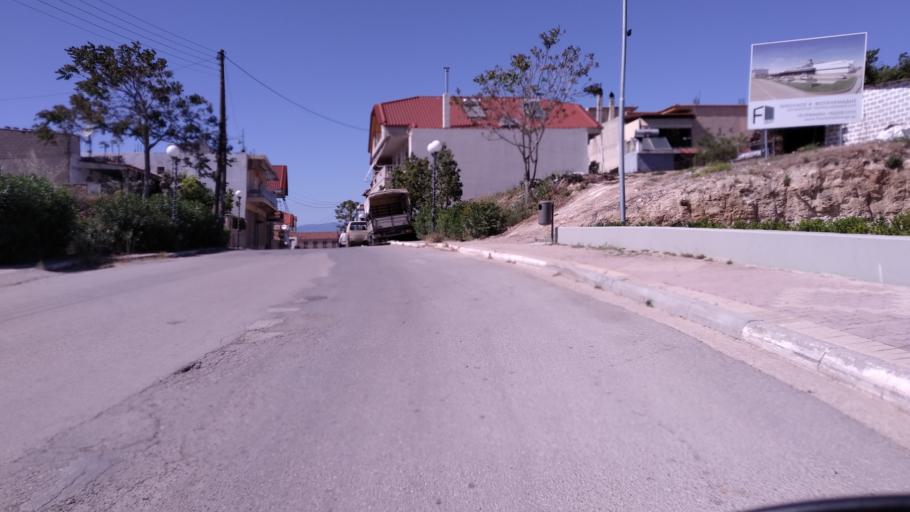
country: GR
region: Central Greece
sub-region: Nomos Fthiotidos
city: Malesina
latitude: 38.6206
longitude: 23.2319
